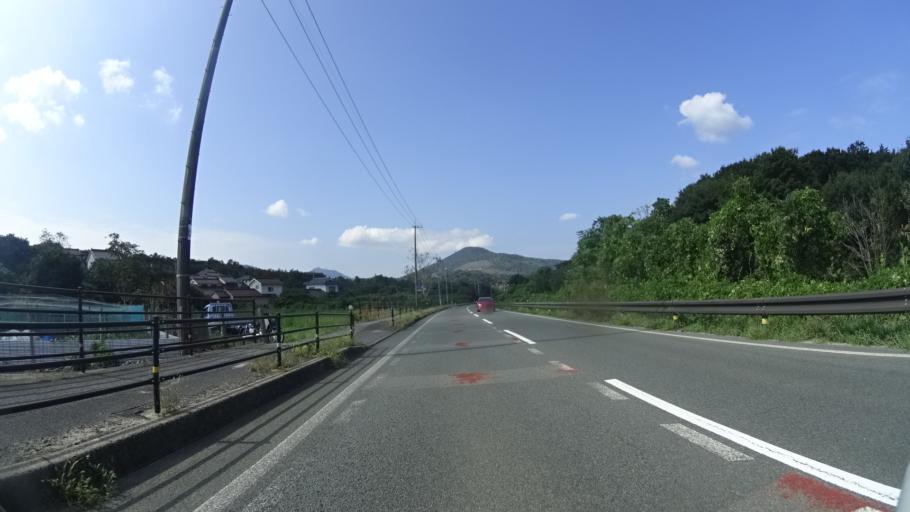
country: JP
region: Shimane
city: Gotsucho
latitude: 35.0385
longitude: 132.2842
